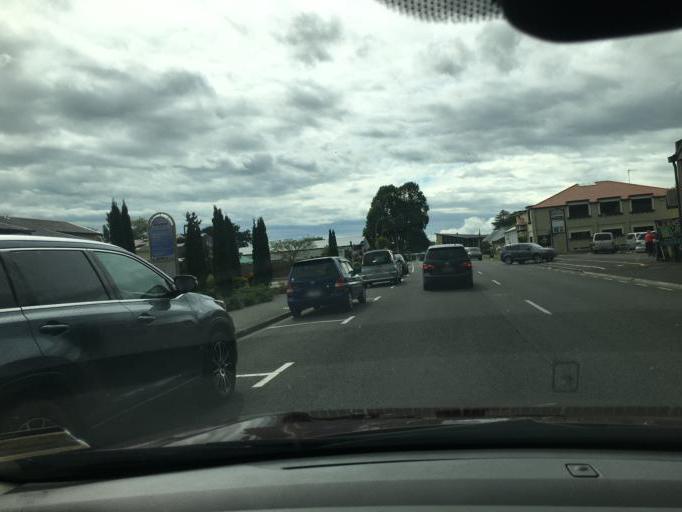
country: NZ
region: Waikato
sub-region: Waipa District
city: Cambridge
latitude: -37.8963
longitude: 175.4704
